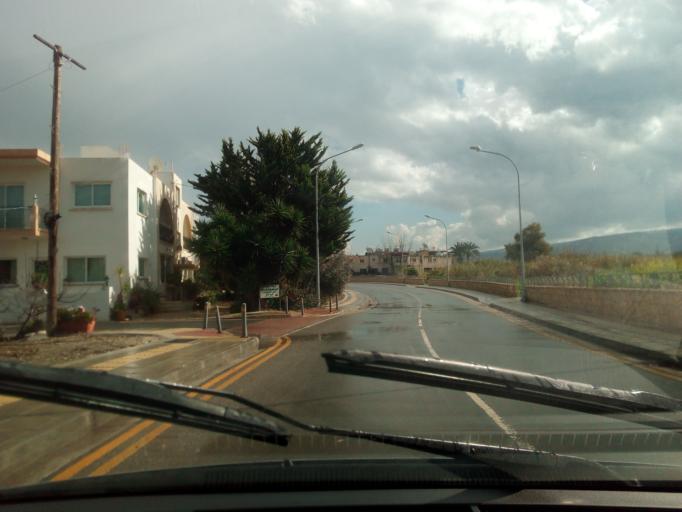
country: CY
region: Pafos
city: Polis
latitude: 35.0330
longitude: 32.4228
